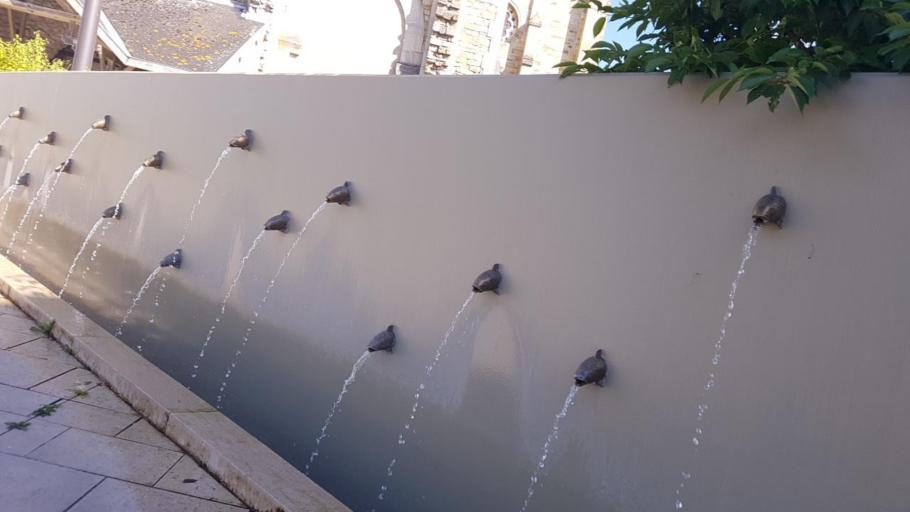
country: FR
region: Lorraine
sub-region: Departement de la Meuse
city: Bar-le-Duc
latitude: 48.7702
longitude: 5.1660
